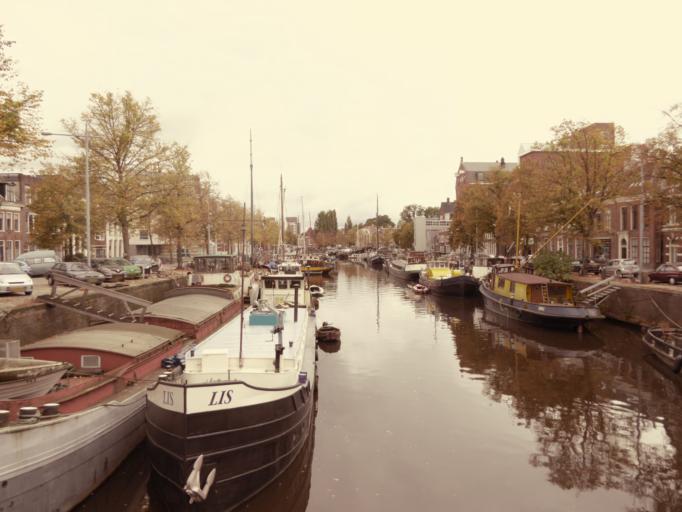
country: NL
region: Groningen
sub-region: Gemeente Groningen
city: Groningen
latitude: 53.2210
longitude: 6.5605
